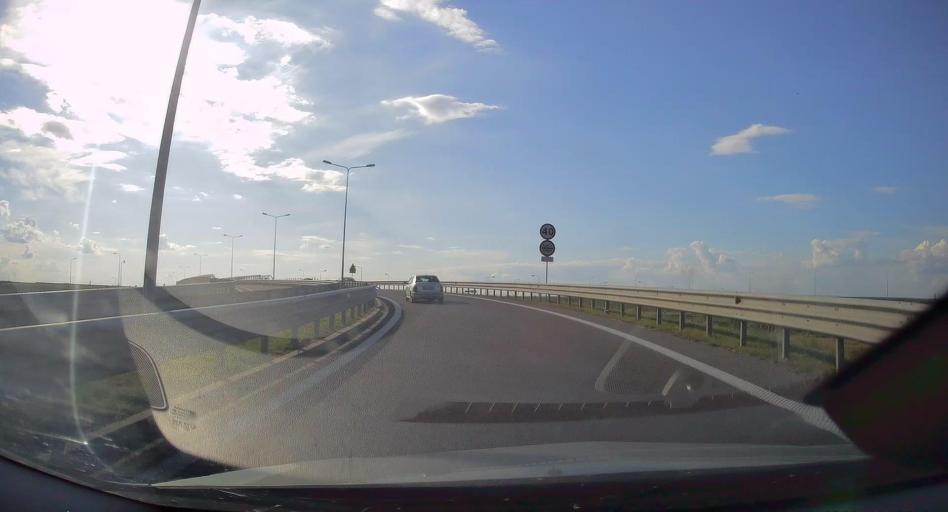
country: PL
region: Subcarpathian Voivodeship
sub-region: Powiat jaroslawski
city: Radymno
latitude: 49.9076
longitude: 22.8197
